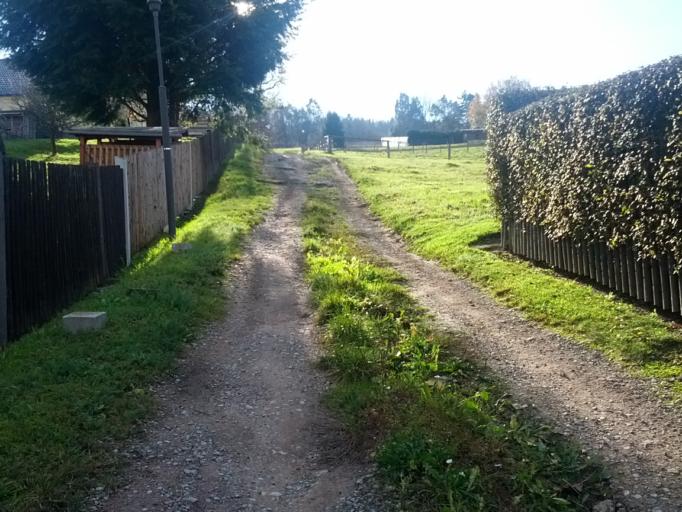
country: DE
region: Thuringia
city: Krauthausen
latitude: 51.0060
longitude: 10.2313
